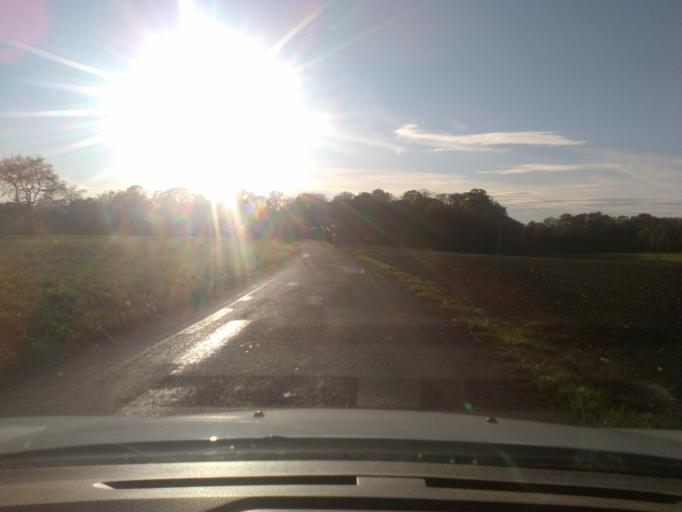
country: FR
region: Lorraine
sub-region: Departement des Vosges
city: Chatel-sur-Moselle
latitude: 48.3217
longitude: 6.4328
